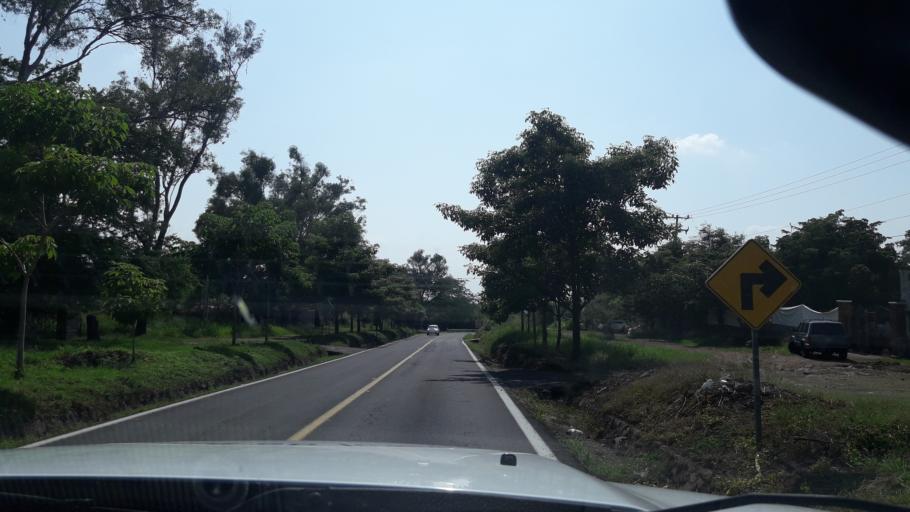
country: MX
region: Colima
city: Comala
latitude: 19.3329
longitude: -103.7481
